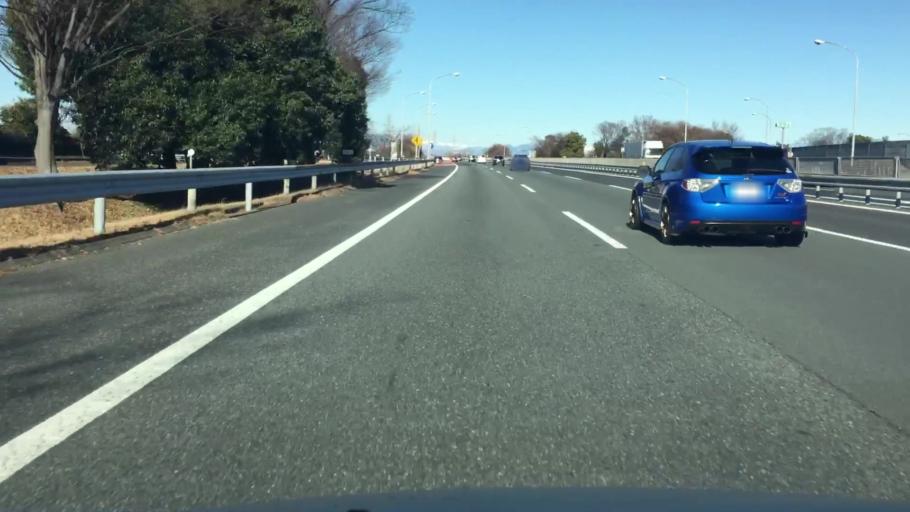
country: JP
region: Saitama
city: Honjo
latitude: 36.2176
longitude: 139.1646
